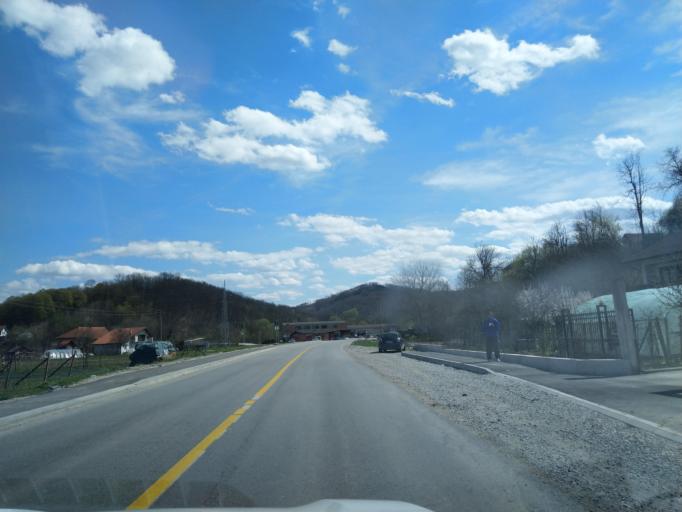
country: RS
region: Central Serbia
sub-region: Zlatiborski Okrug
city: Arilje
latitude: 43.7867
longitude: 20.1077
